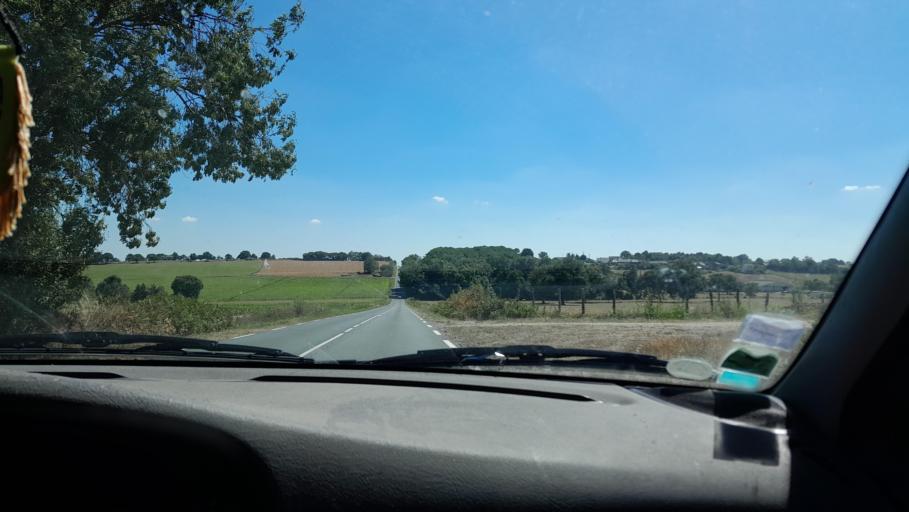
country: FR
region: Pays de la Loire
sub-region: Departement de la Loire-Atlantique
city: Saint-Mars-la-Jaille
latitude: 47.5522
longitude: -1.1854
